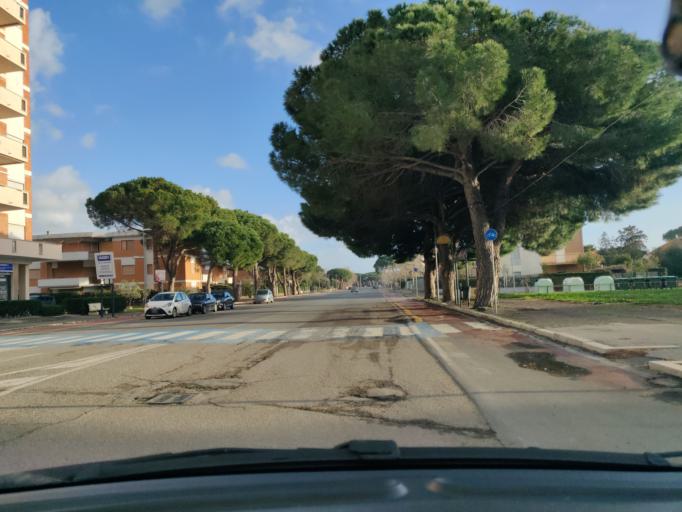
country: IT
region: Latium
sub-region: Provincia di Viterbo
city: Tarquinia
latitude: 42.2245
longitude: 11.7072
